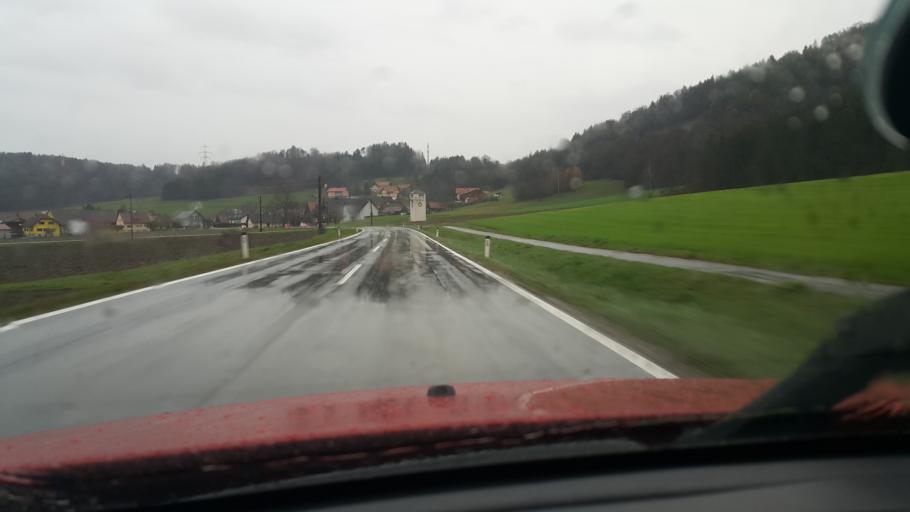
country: AT
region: Styria
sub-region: Politischer Bezirk Leibnitz
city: Wildon
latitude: 46.8660
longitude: 15.4901
